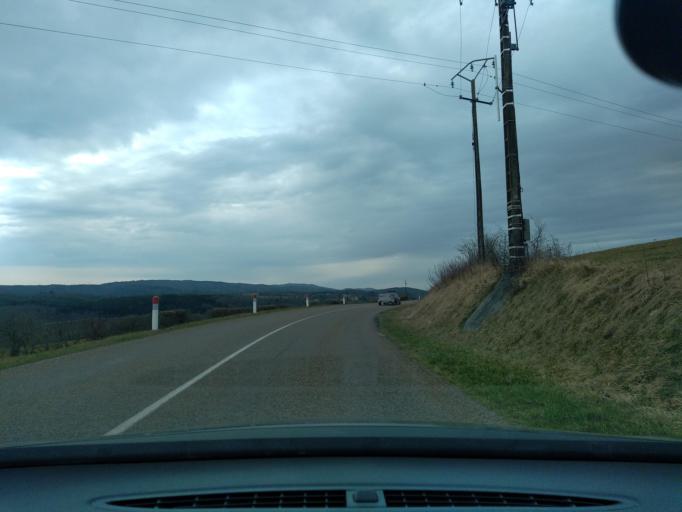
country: FR
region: Franche-Comte
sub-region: Departement du Jura
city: Orgelet
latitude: 46.5121
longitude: 5.6065
